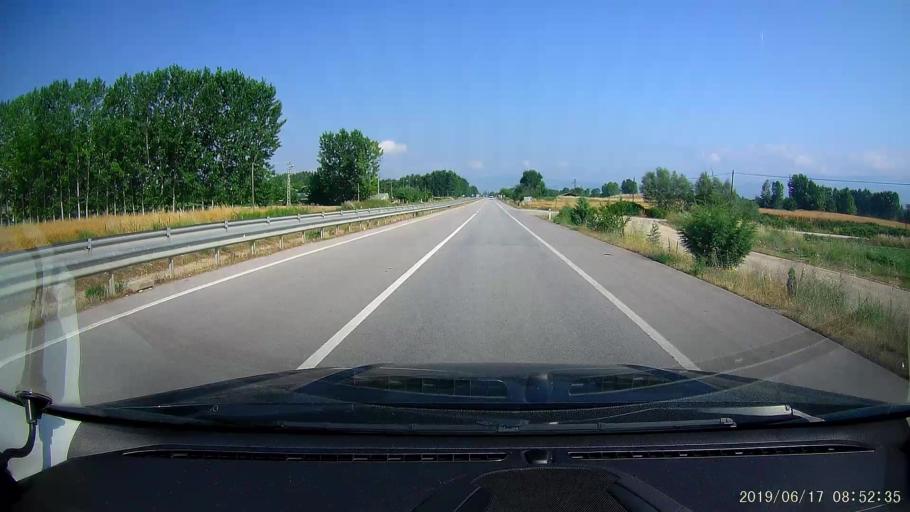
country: TR
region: Tokat
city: Erbaa
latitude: 40.6997
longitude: 36.4943
